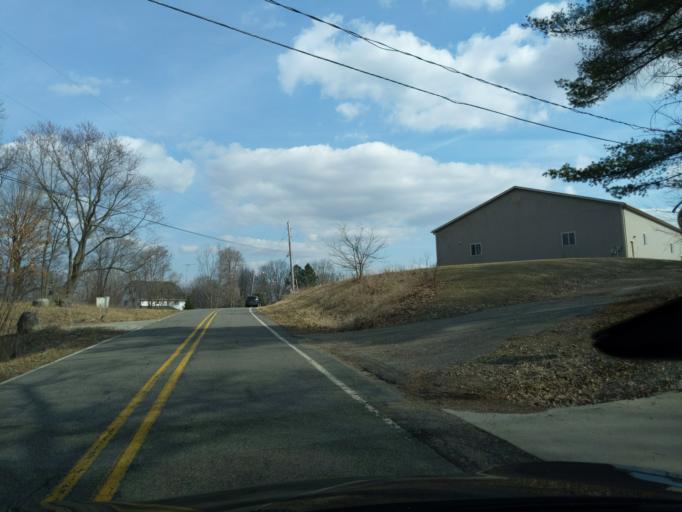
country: US
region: Michigan
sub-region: Ingham County
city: Leslie
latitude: 42.3648
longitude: -84.4221
